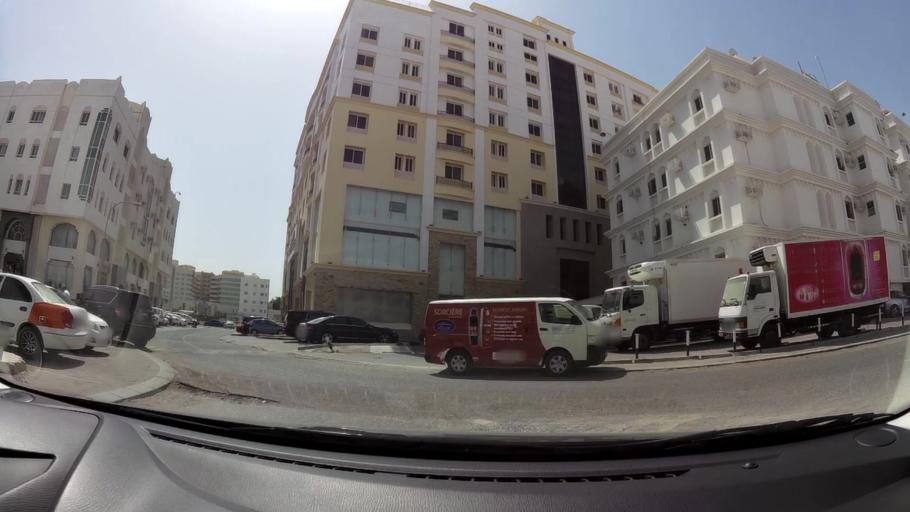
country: OM
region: Muhafazat Masqat
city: Bawshar
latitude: 23.5892
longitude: 58.4273
